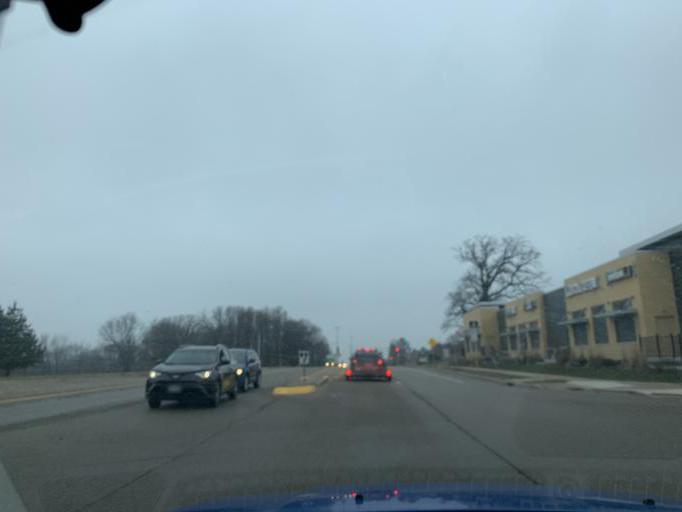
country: US
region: Wisconsin
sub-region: Dane County
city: Monona
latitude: 43.0847
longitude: -89.2778
